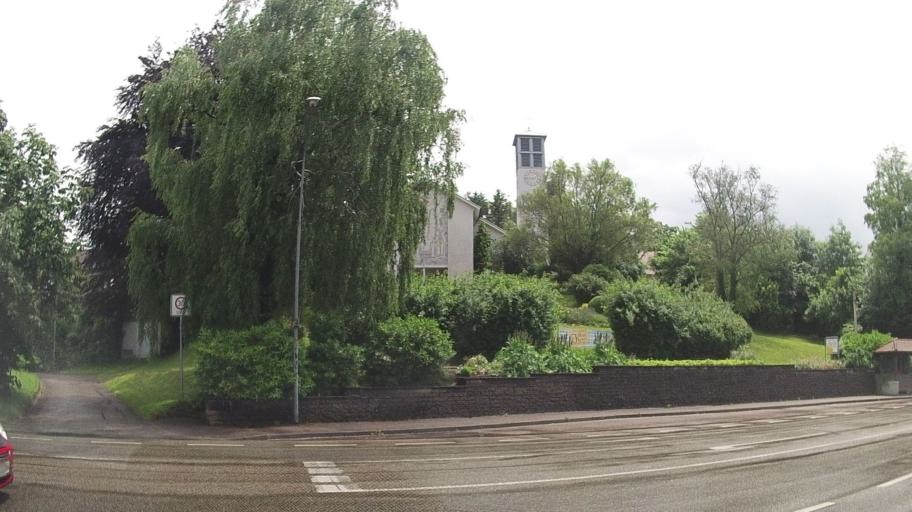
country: DE
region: Baden-Wuerttemberg
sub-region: Freiburg Region
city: Achern
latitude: 48.6247
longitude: 8.0494
